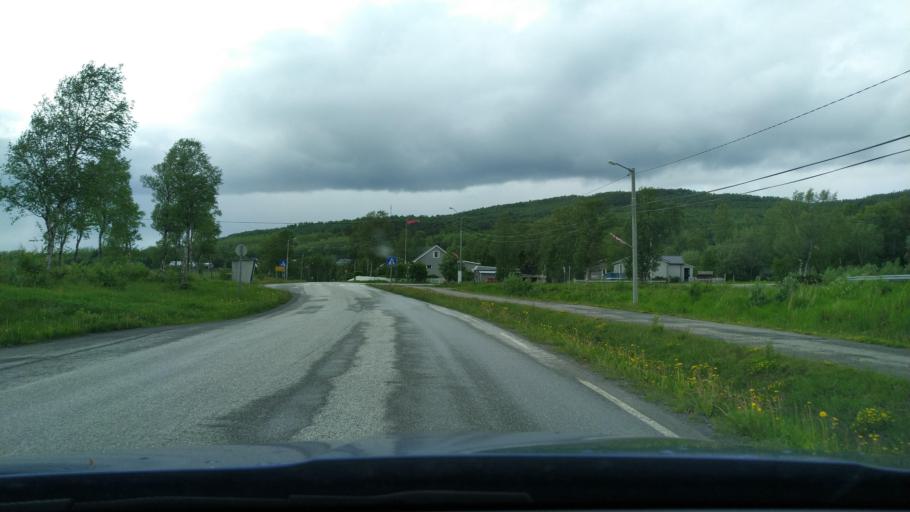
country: NO
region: Troms
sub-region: Dyroy
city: Brostadbotn
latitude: 69.0879
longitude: 17.6946
